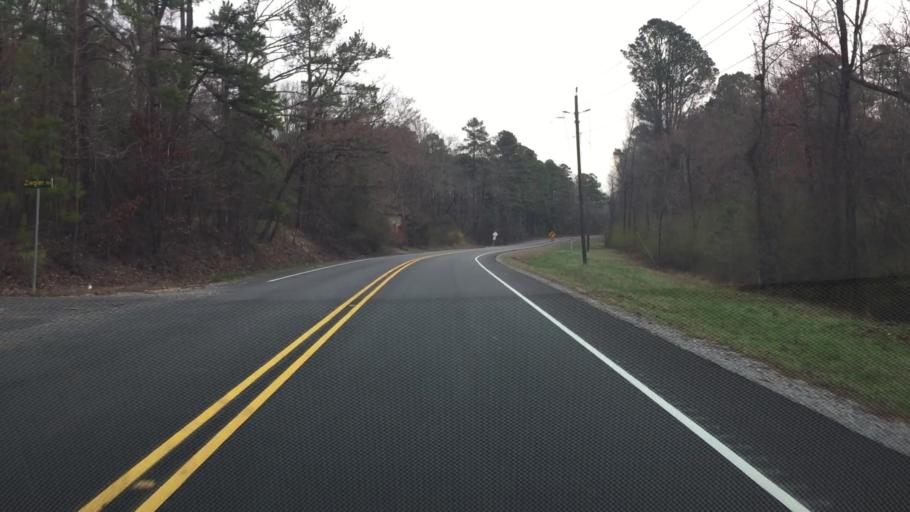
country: US
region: Arkansas
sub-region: Saline County
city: Haskell
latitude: 34.6154
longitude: -92.7885
